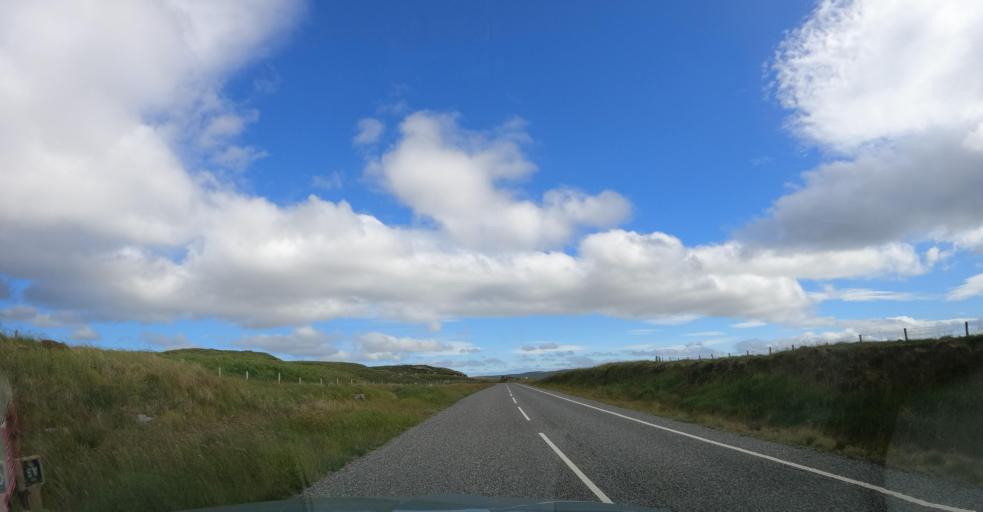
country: GB
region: Scotland
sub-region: Eilean Siar
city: Harris
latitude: 58.1952
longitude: -6.7178
